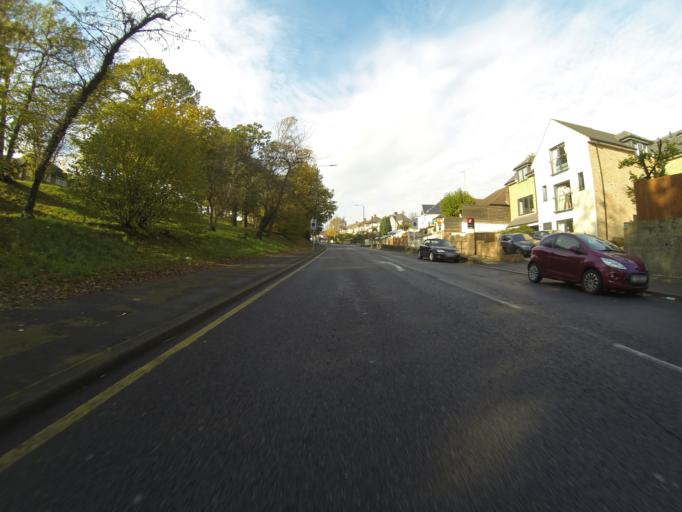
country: GB
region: England
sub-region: Greater London
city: Bexley
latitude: 51.4538
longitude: 0.1606
